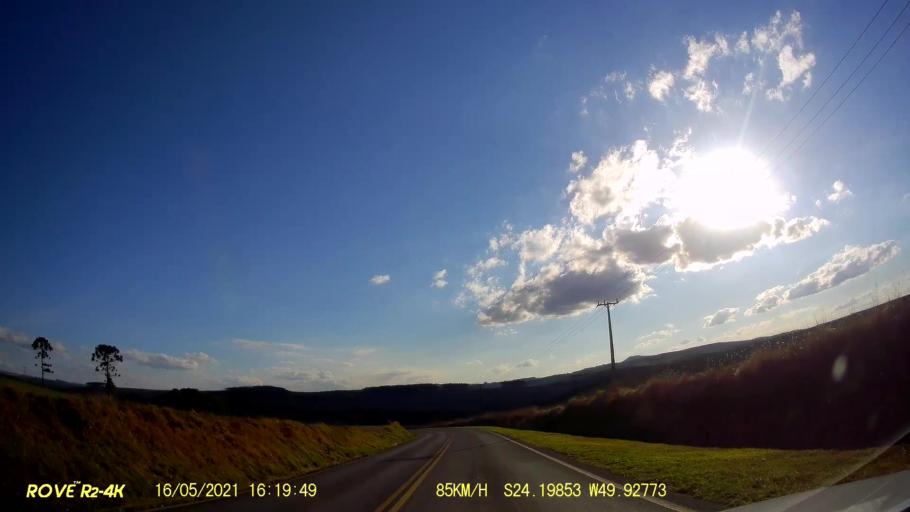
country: BR
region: Parana
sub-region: Jaguariaiva
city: Jaguariaiva
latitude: -24.1992
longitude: -49.9273
